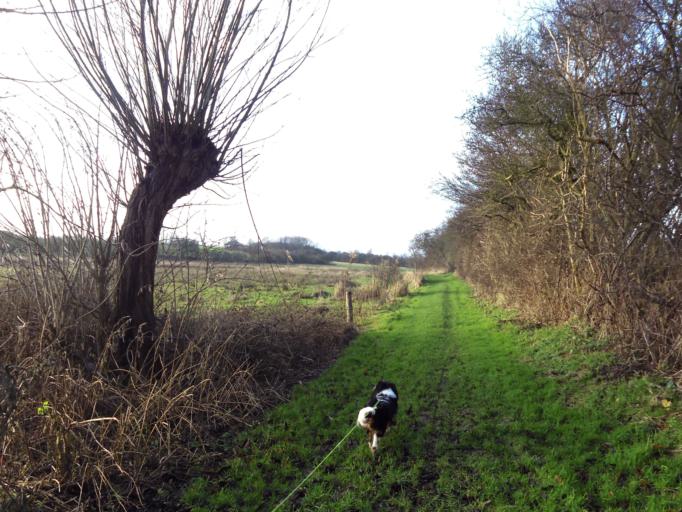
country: DK
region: South Denmark
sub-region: Sonderborg Kommune
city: Dybbol
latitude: 54.9610
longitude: 9.7276
